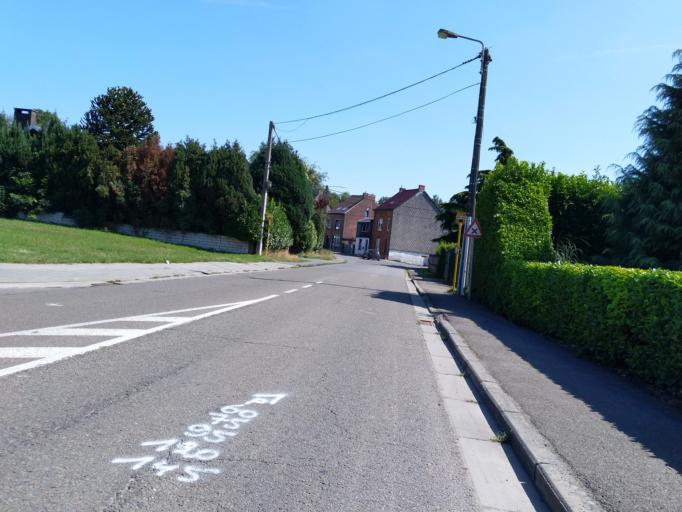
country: BE
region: Wallonia
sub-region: Province du Hainaut
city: Roeulx
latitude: 50.4748
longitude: 4.1079
